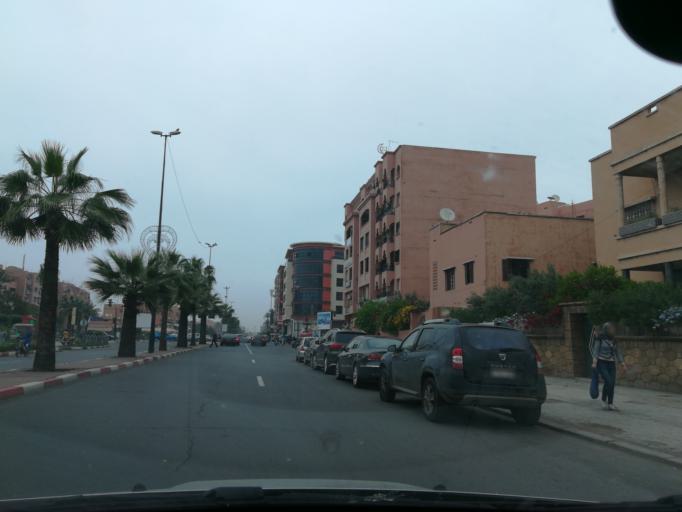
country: MA
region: Marrakech-Tensift-Al Haouz
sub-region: Marrakech
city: Marrakesh
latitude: 31.6397
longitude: -7.9998
